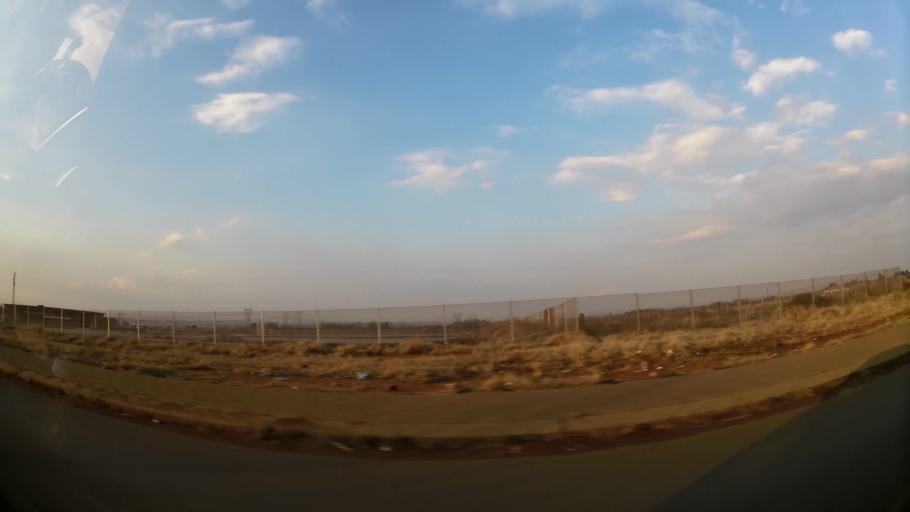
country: ZA
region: Gauteng
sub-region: City of Johannesburg Metropolitan Municipality
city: Orange Farm
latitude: -26.5629
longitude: 27.8612
